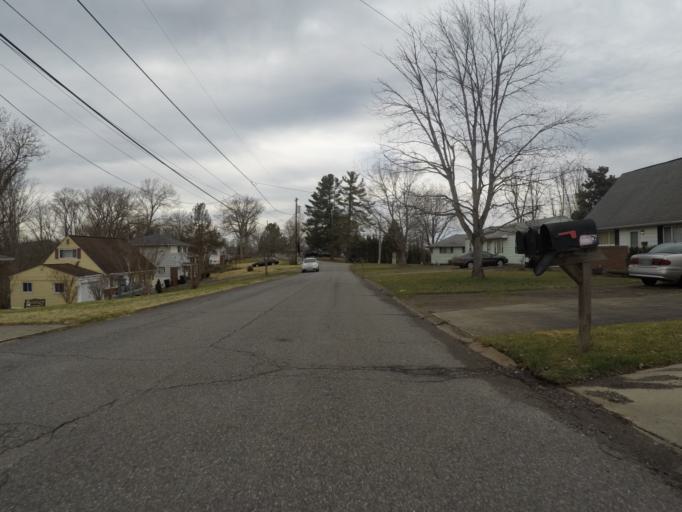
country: US
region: West Virginia
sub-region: Cabell County
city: Pea Ridge
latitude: 38.3962
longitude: -82.3831
